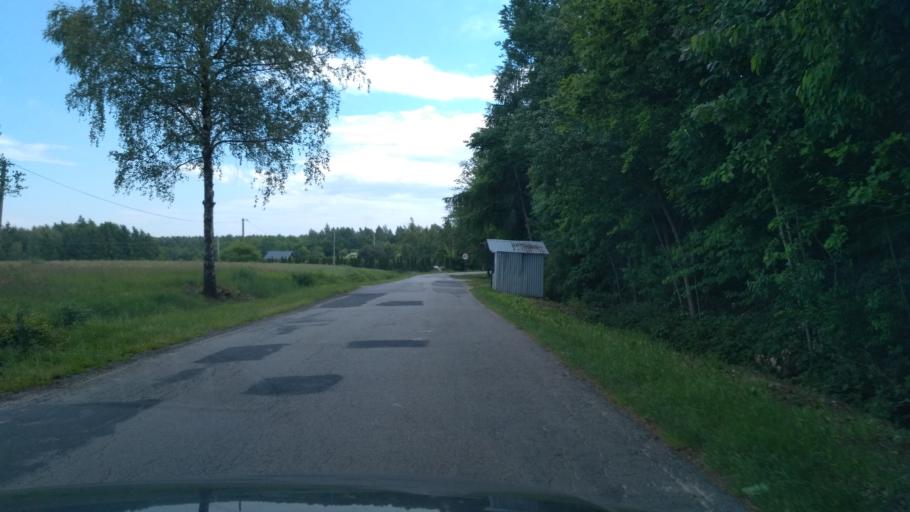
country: PL
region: Subcarpathian Voivodeship
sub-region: Powiat ropczycko-sedziszowski
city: Ropczyce
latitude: 50.0161
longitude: 21.6096
